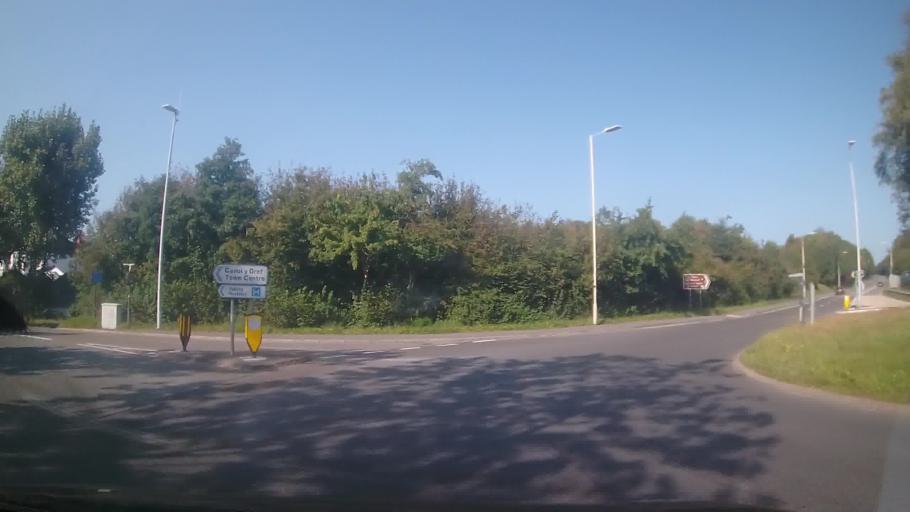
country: GB
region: Wales
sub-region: County of Ceredigion
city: Cardigan
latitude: 52.0826
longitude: -4.6536
